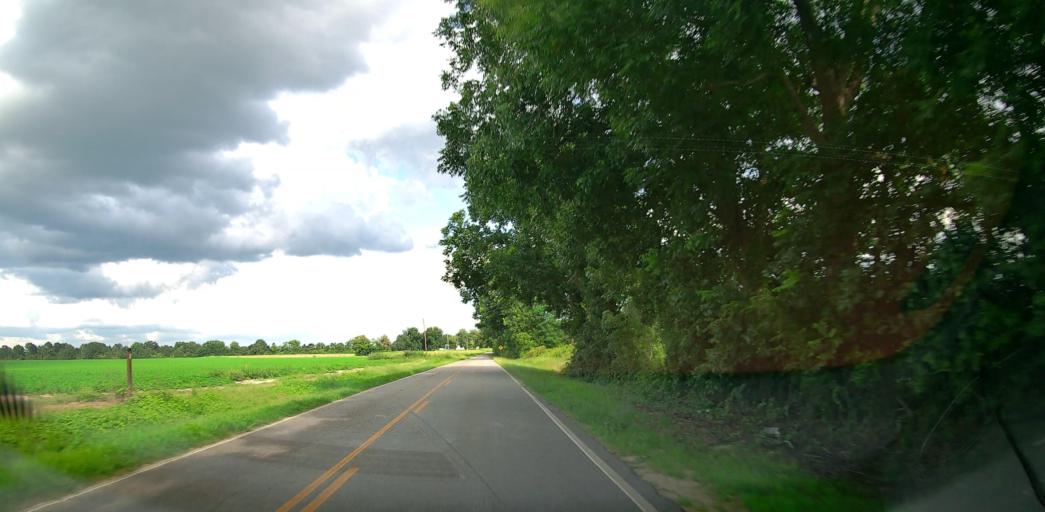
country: US
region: Georgia
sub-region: Bleckley County
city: Cochran
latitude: 32.4078
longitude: -83.3853
